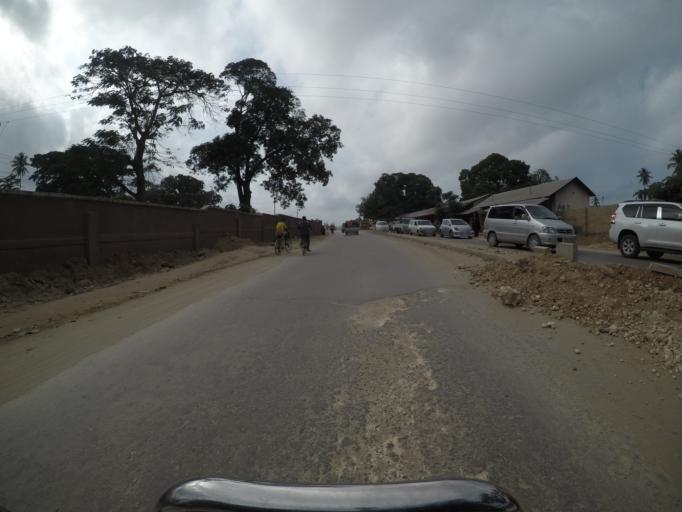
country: TZ
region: Zanzibar Urban/West
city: Zanzibar
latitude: -6.1807
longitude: 39.2298
